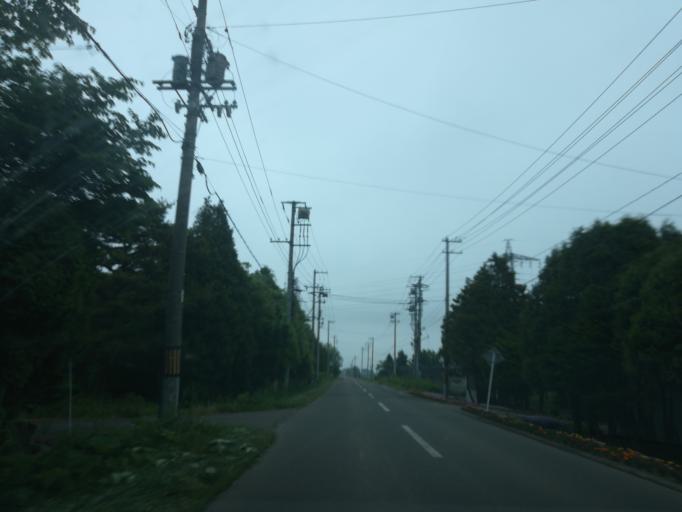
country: JP
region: Hokkaido
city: Ebetsu
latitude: 43.0610
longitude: 141.6242
